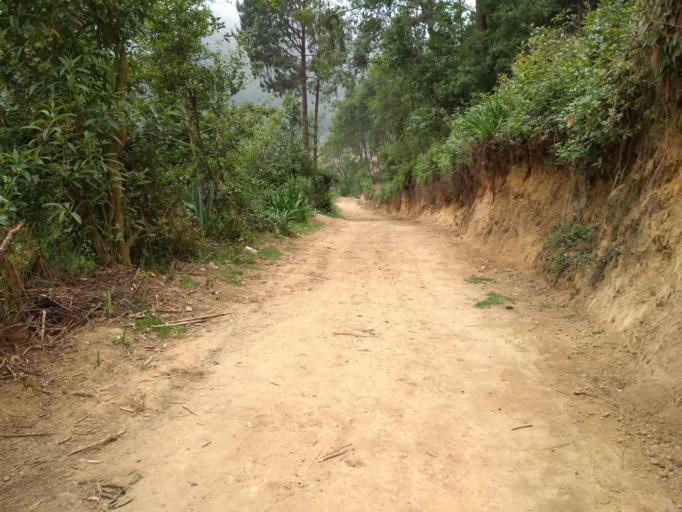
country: MX
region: Veracruz
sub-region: Mariano Escobedo
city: San Isidro el Berro
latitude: 18.9477
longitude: -97.2038
